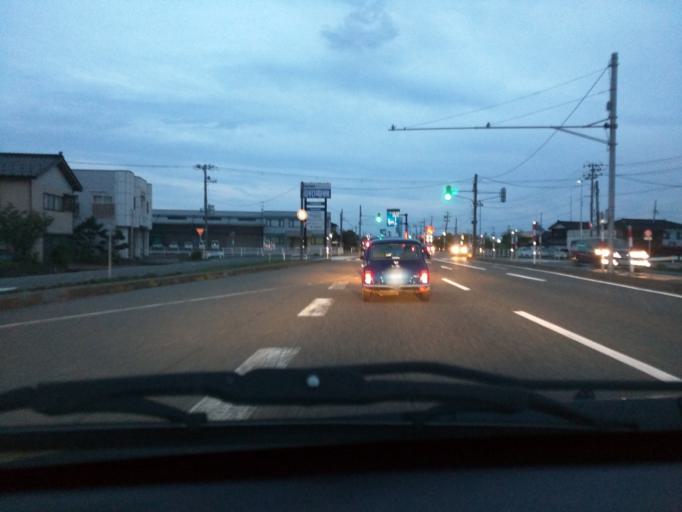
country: JP
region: Niigata
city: Kashiwazaki
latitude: 37.3622
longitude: 138.5854
